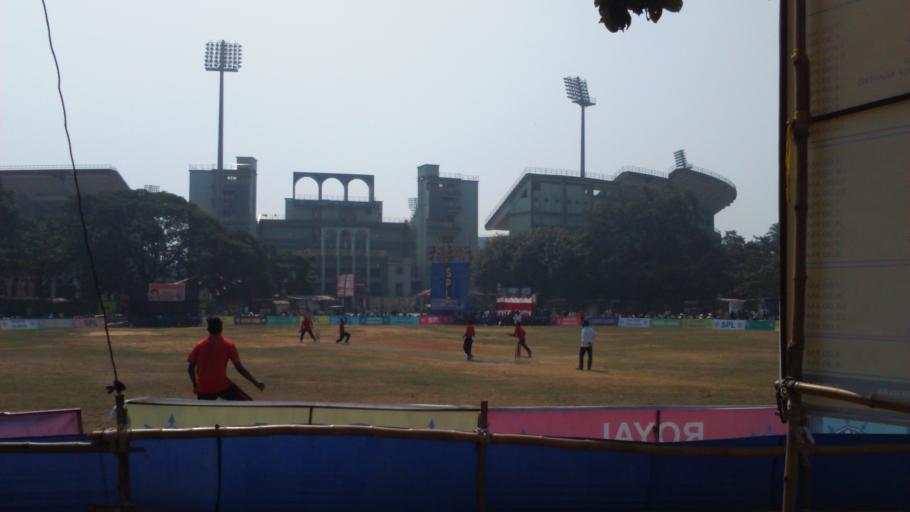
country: IN
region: Odisha
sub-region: Cuttack
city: Cuttack
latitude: 20.4832
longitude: 85.8686
